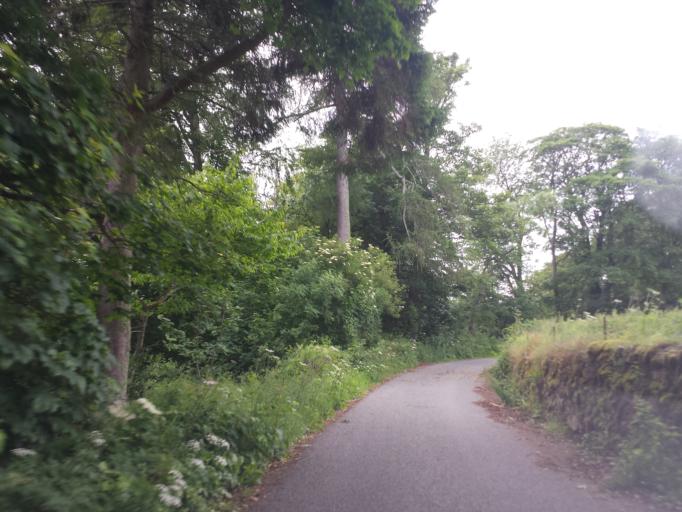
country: GB
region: Scotland
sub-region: Highland
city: Fortrose
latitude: 57.5059
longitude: -4.0075
